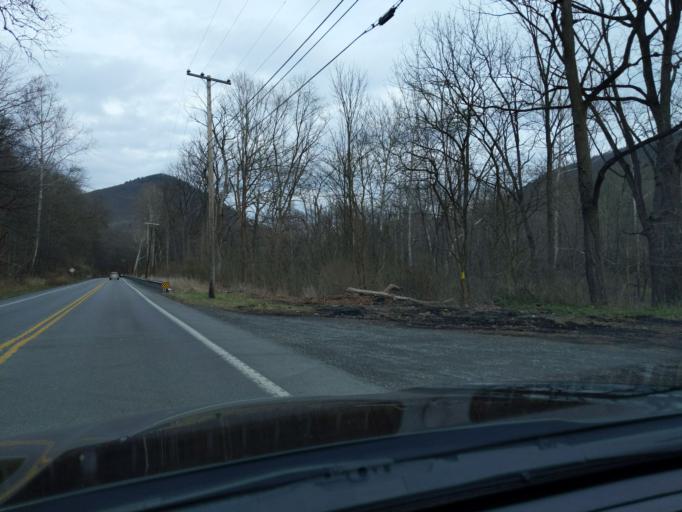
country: US
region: Pennsylvania
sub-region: Blair County
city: Williamsburg
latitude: 40.4768
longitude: -78.2641
